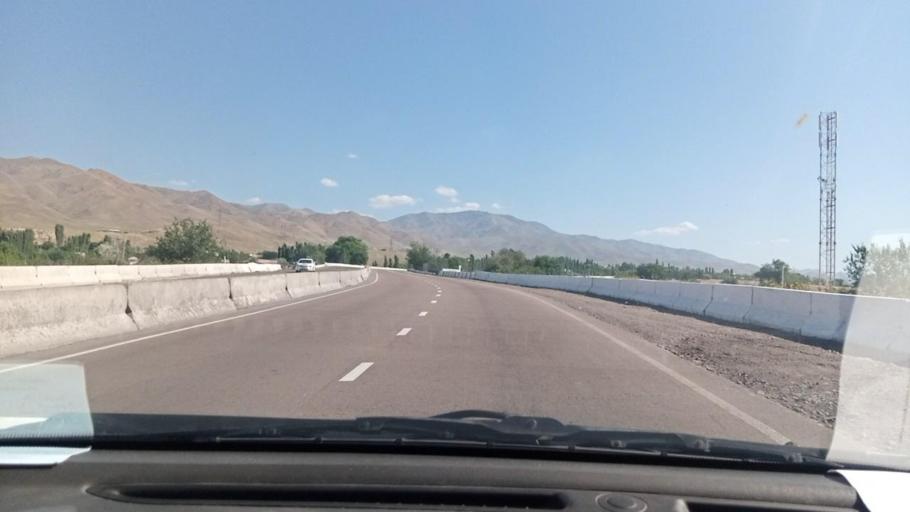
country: UZ
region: Toshkent
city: Angren
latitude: 40.9432
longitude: 69.9070
